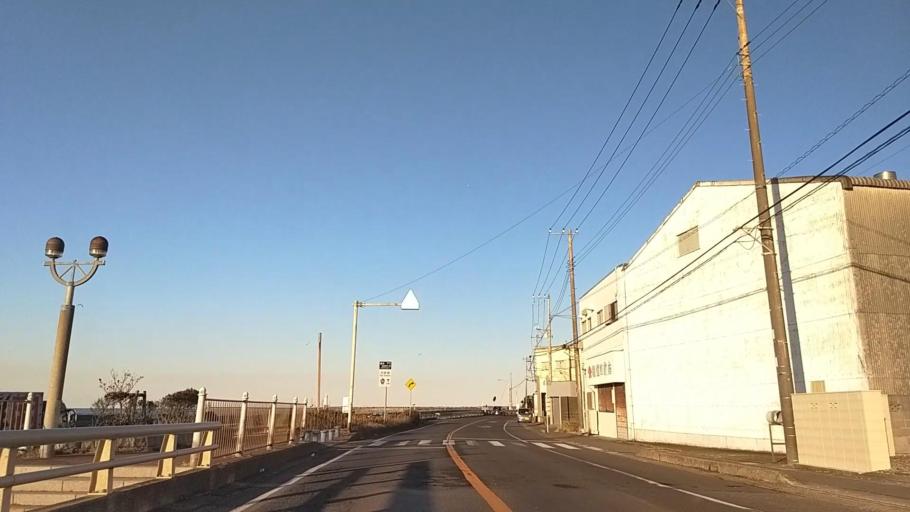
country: JP
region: Chiba
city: Hasaki
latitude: 35.7414
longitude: 140.8548
